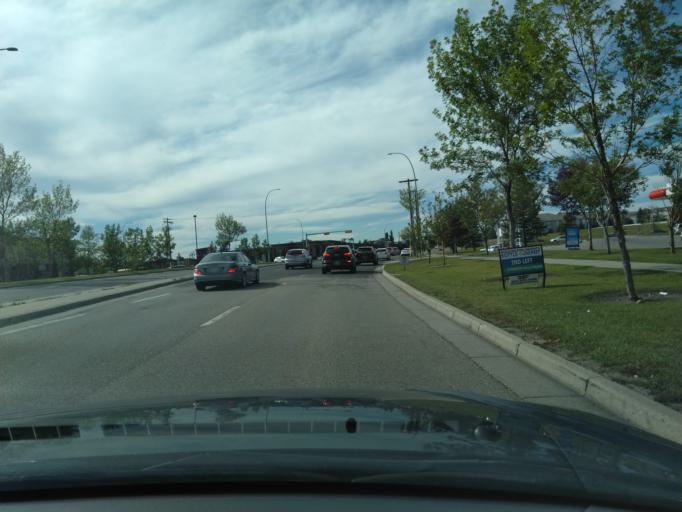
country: CA
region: Alberta
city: Calgary
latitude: 51.1419
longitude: -114.0674
